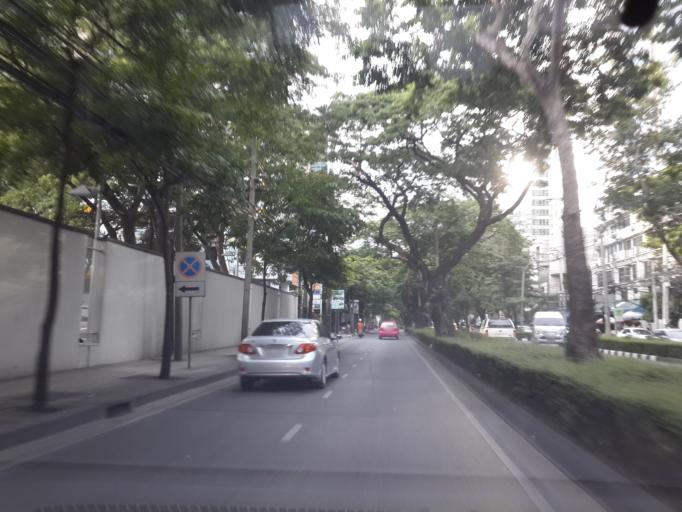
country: TH
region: Bangkok
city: Pathum Wan
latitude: 13.7375
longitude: 100.5464
